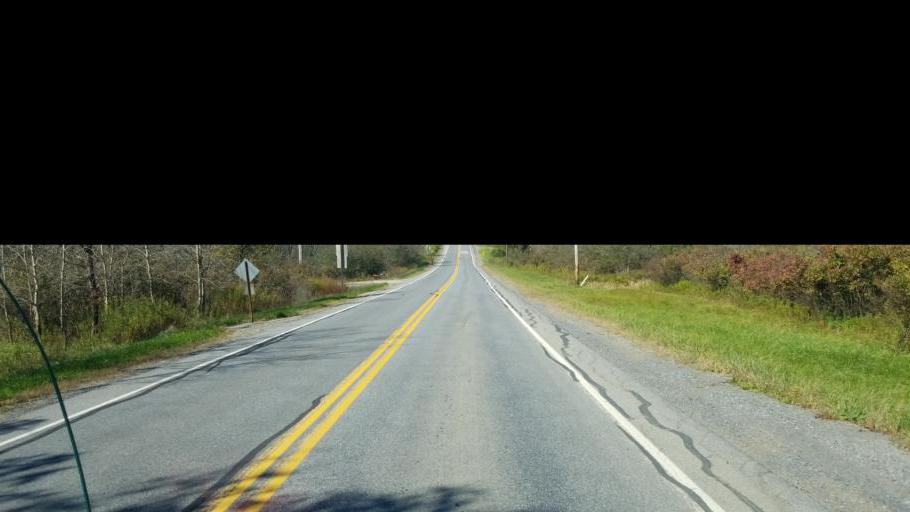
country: US
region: Pennsylvania
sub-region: Somerset County
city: Central City
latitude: 40.0376
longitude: -78.7652
